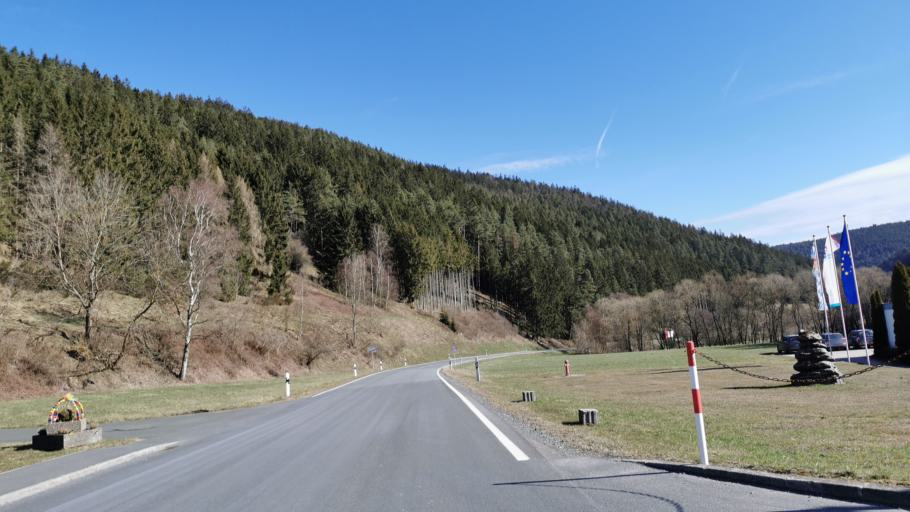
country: DE
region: Bavaria
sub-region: Upper Franconia
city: Ludwigsstadt
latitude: 50.4921
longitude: 11.3531
